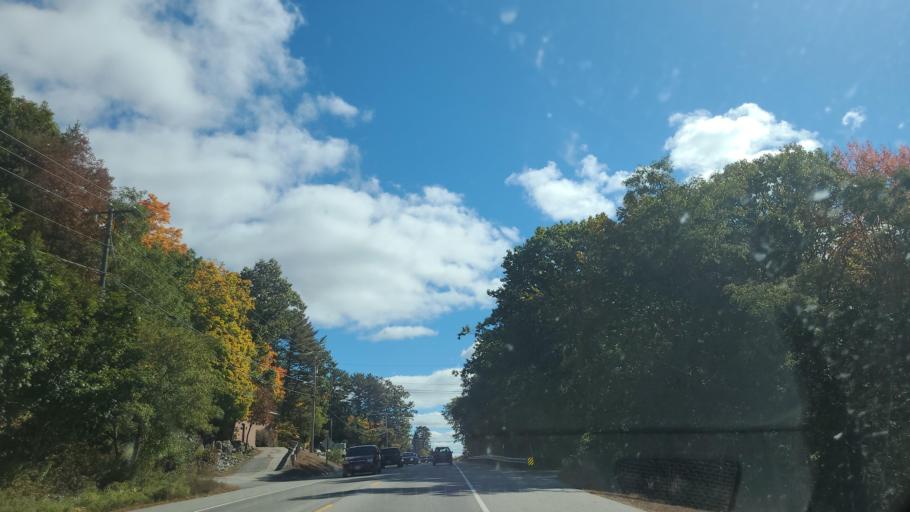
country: US
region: Maine
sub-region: Cumberland County
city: Raymond
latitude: 43.9688
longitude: -70.5896
